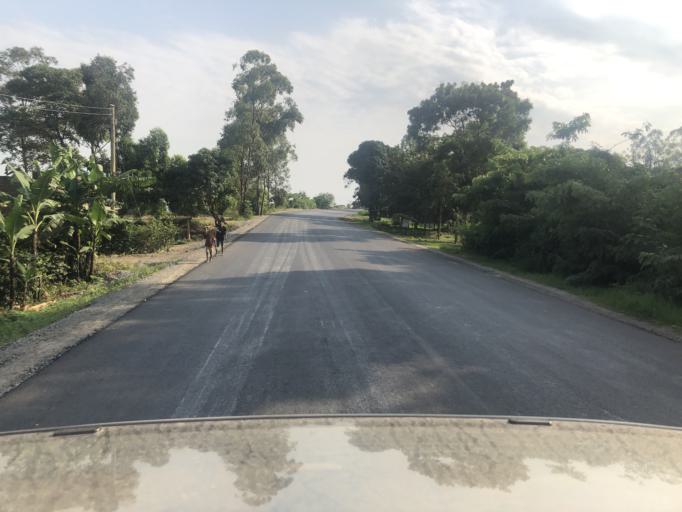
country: UG
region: Western Region
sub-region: Rubirizi District
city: Rubirizi
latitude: -0.2272
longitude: 30.0939
